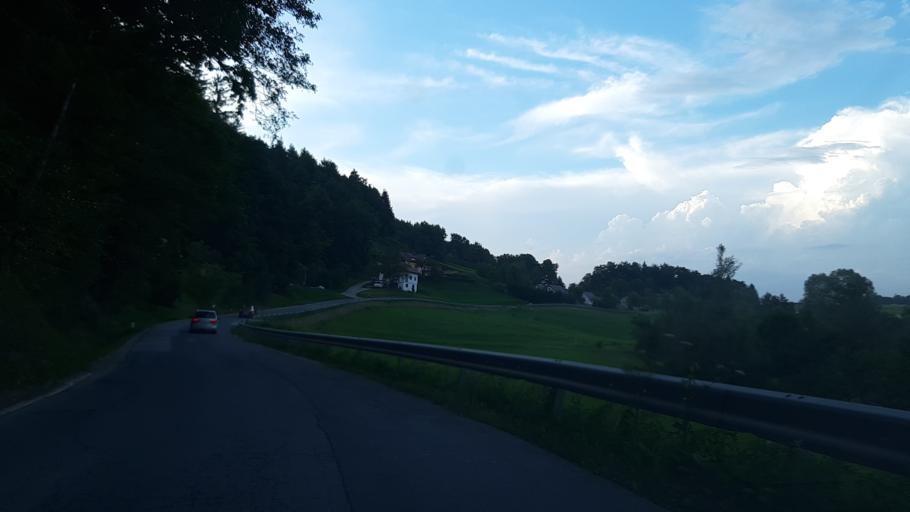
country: SI
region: Sentjur pri Celju
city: Sentjur
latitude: 46.1930
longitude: 15.4281
